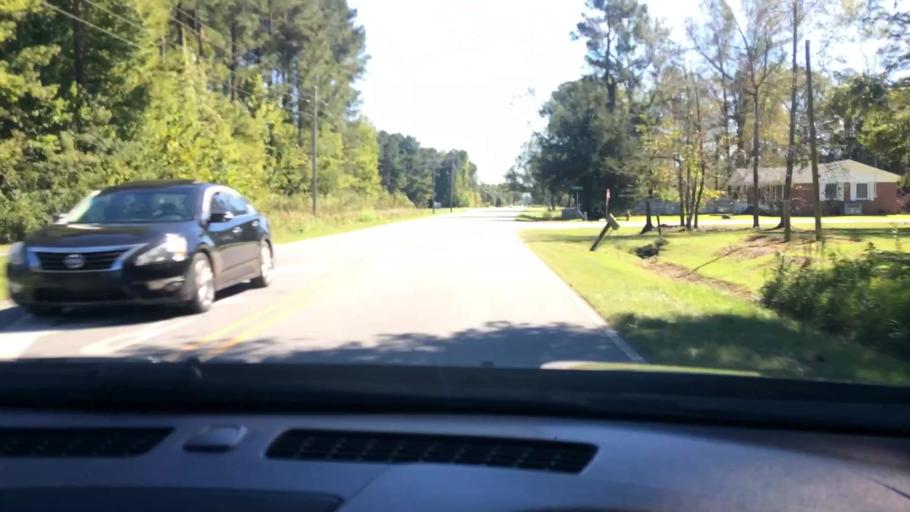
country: US
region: North Carolina
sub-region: Pitt County
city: Grifton
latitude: 35.4065
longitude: -77.4245
